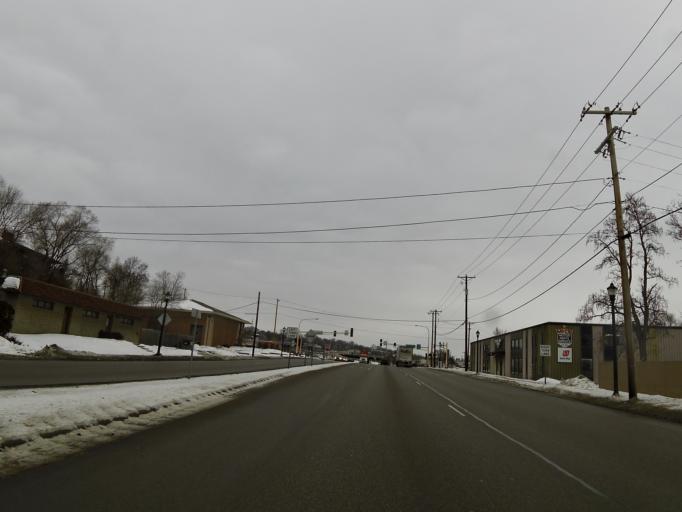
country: US
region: Minnesota
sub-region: Dakota County
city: South Saint Paul
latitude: 44.8719
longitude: -93.0283
